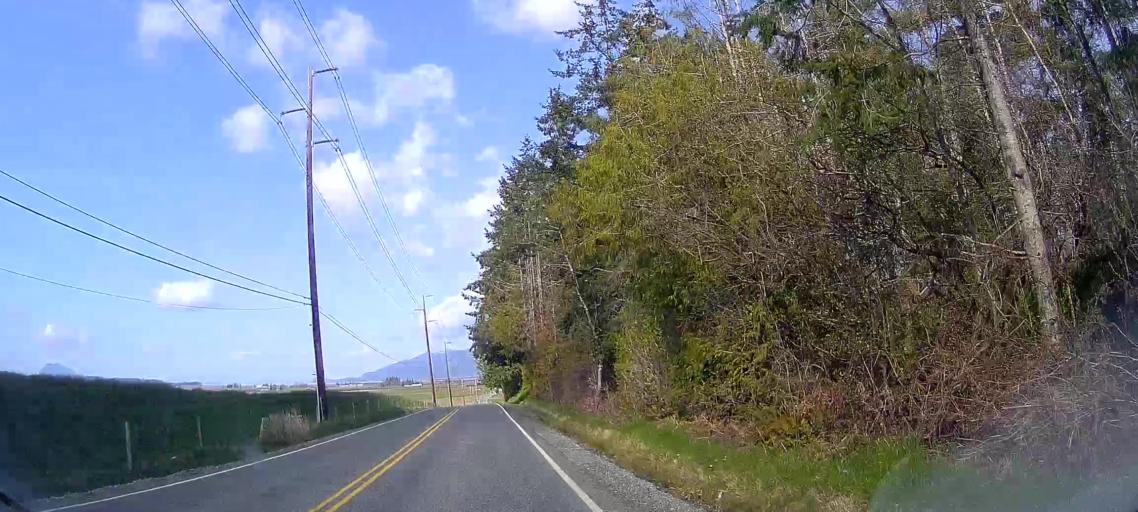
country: US
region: Washington
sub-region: Skagit County
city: Burlington
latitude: 48.5092
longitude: -122.4444
